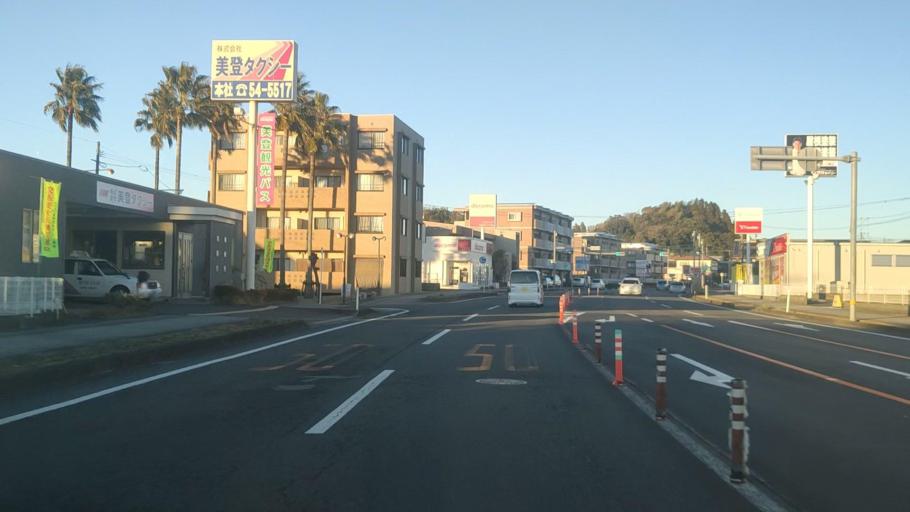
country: JP
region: Miyazaki
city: Miyazaki-shi
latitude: 31.9019
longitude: 131.4059
